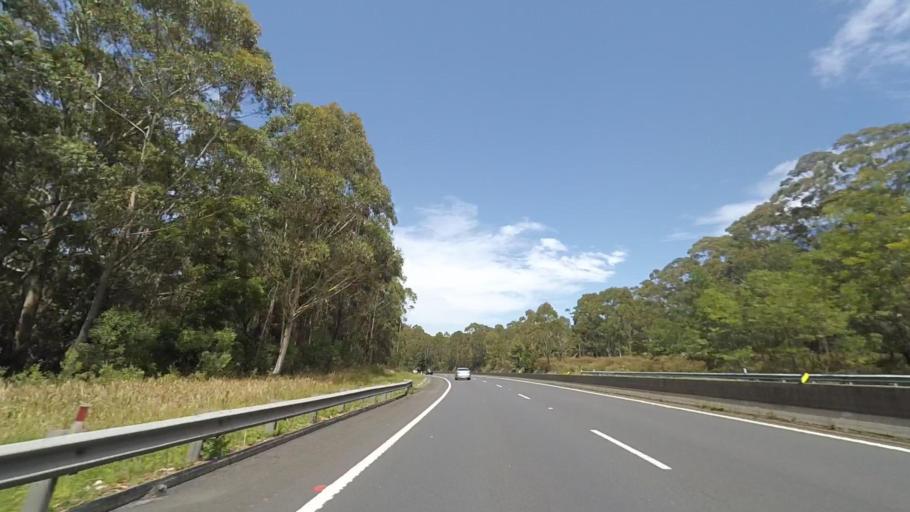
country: AU
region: New South Wales
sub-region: Wollongong
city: Bulli
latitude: -34.3263
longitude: 150.8768
